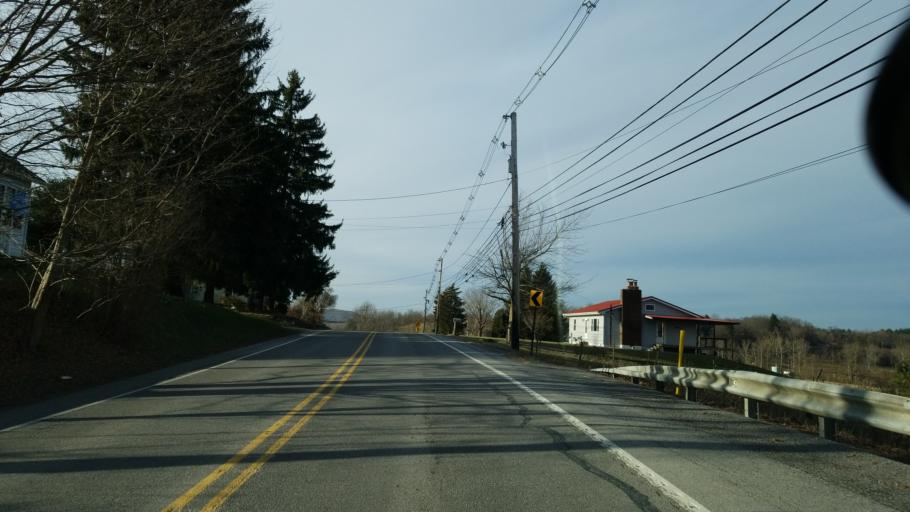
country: US
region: Pennsylvania
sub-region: Clearfield County
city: Curwensville
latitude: 40.9793
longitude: -78.6235
